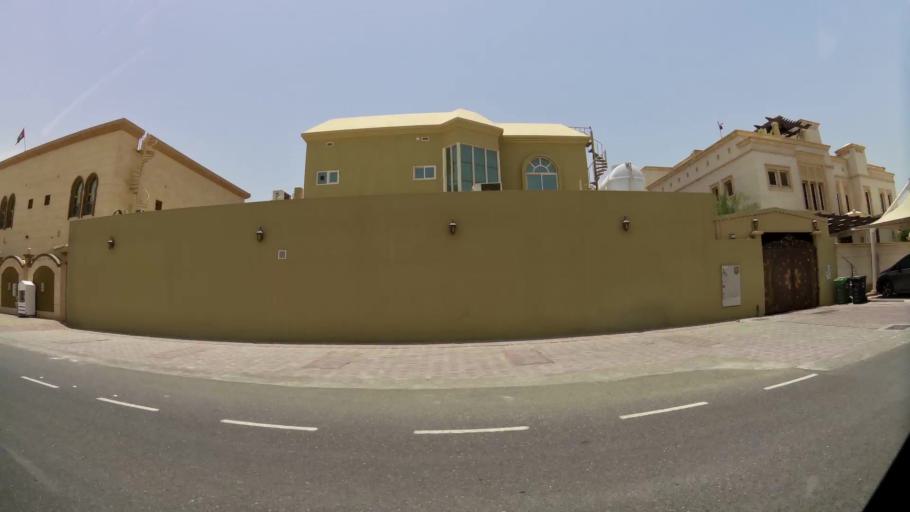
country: AE
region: Ash Shariqah
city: Sharjah
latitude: 25.2063
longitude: 55.3776
